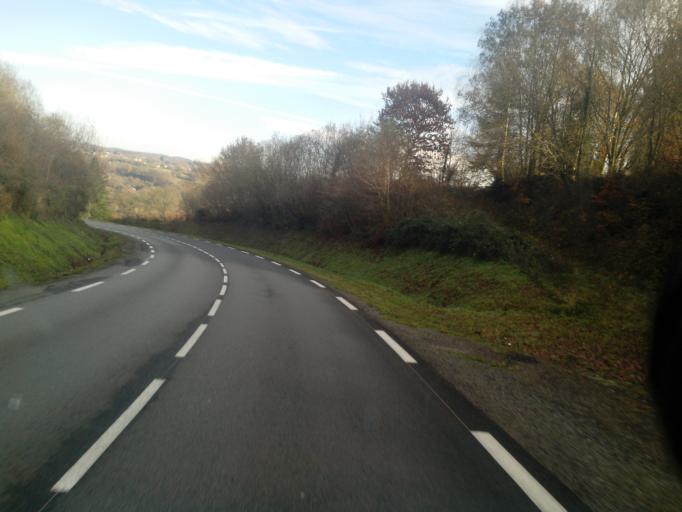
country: FR
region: Limousin
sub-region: Departement de la Haute-Vienne
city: Linards
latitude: 45.7655
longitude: 1.5416
